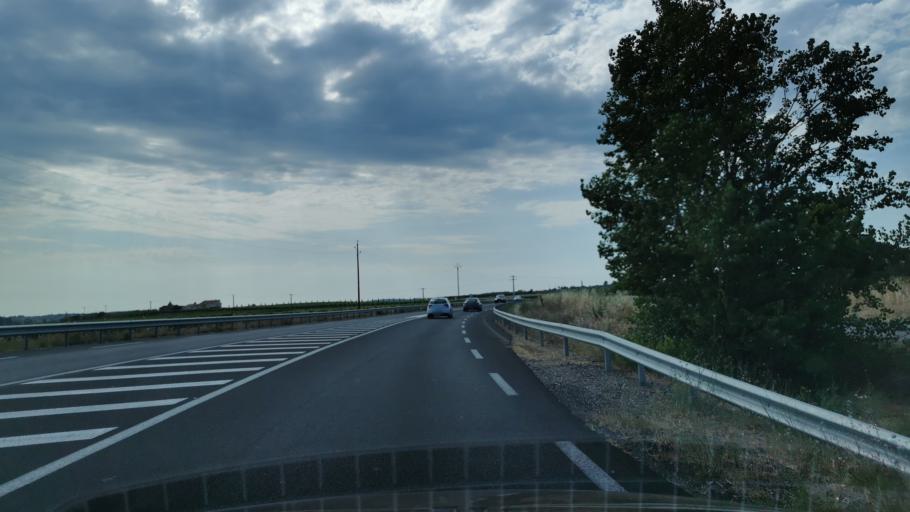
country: FR
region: Languedoc-Roussillon
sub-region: Departement de l'Herault
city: Puisserguier
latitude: 43.3653
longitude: 3.0721
